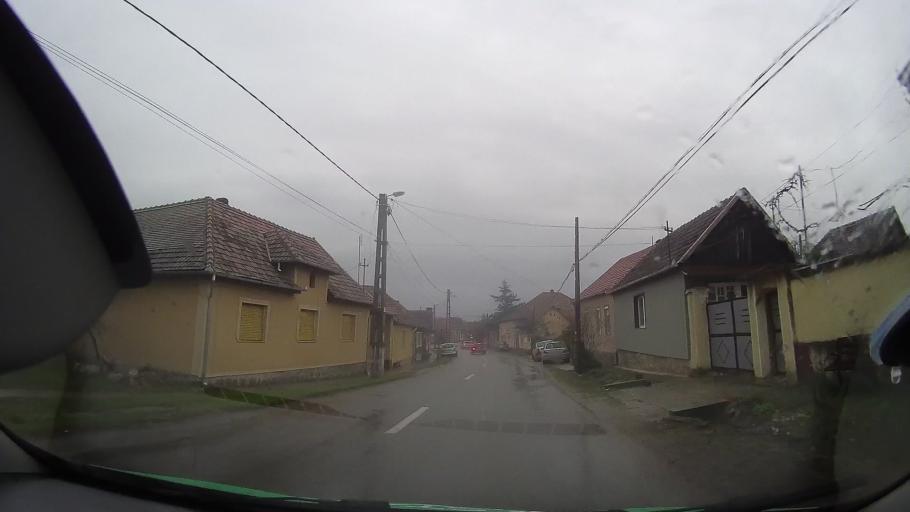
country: RO
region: Bihor
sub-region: Comuna Cociuba Mare
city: Cociuba Mare
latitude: 46.7391
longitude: 21.9970
